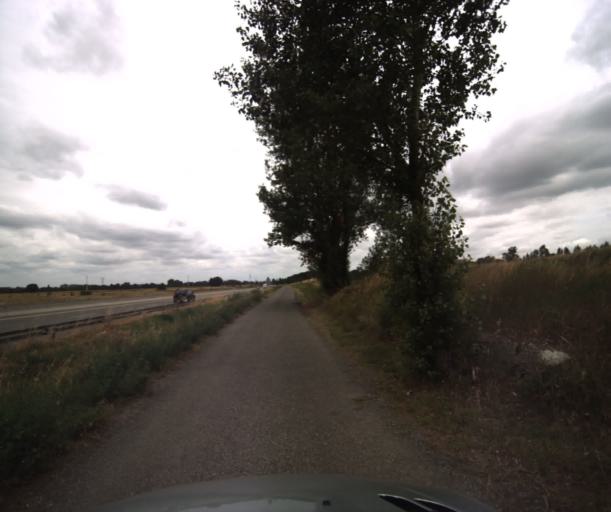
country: FR
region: Midi-Pyrenees
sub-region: Departement de la Haute-Garonne
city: Pinsaguel
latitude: 43.4987
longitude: 1.3882
